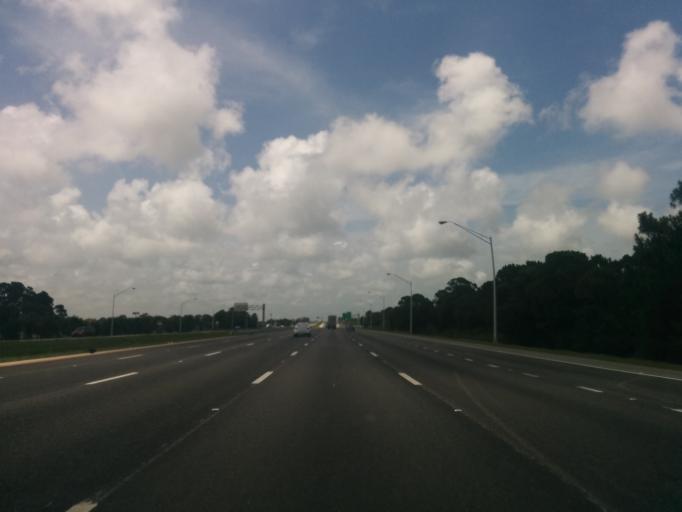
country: US
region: Florida
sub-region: Saint Lucie County
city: Fort Pierce South
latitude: 27.4061
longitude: -80.3882
